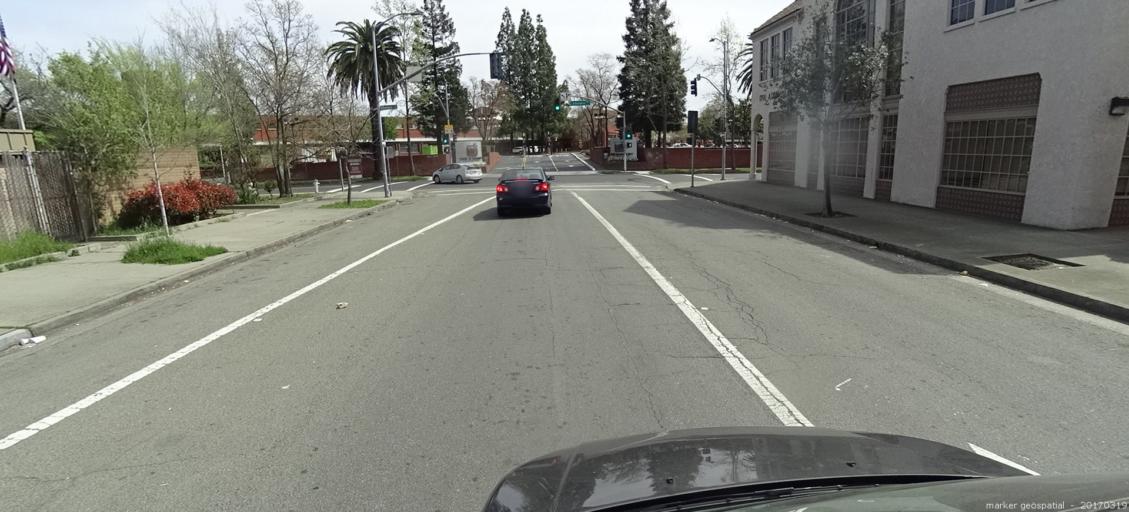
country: US
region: California
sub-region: Sacramento County
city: Sacramento
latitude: 38.5652
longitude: -121.4691
